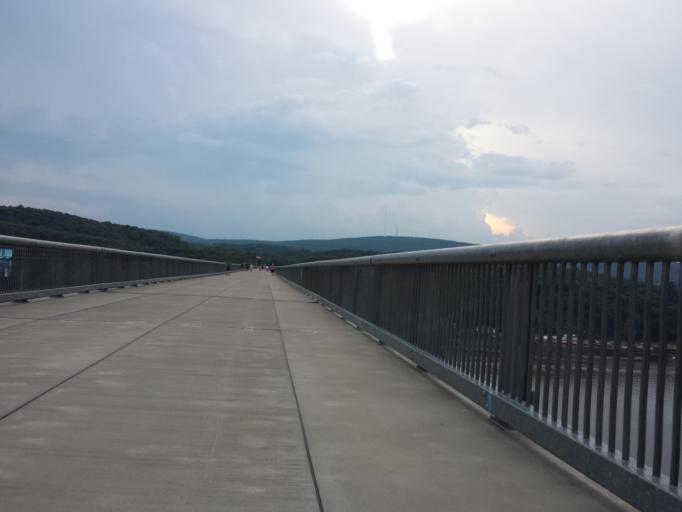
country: US
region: New York
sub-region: Dutchess County
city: Poughkeepsie
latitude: 41.7106
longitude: -73.9402
